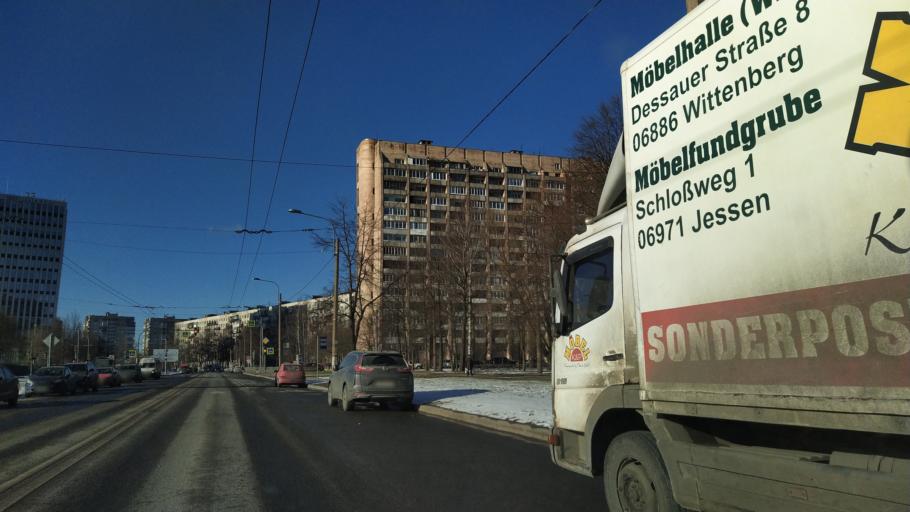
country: RU
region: Leningrad
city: Kalininskiy
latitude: 59.9700
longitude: 30.4246
